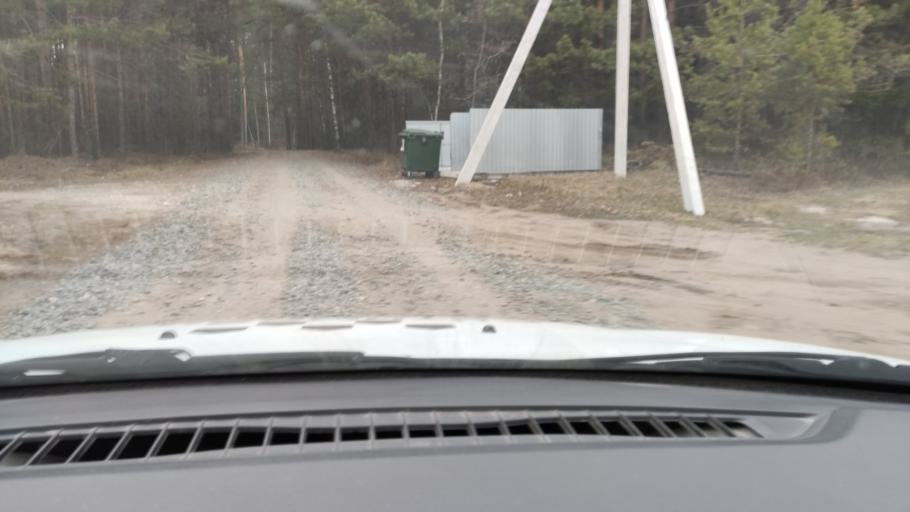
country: RU
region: Perm
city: Perm
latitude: 58.0457
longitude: 56.2057
